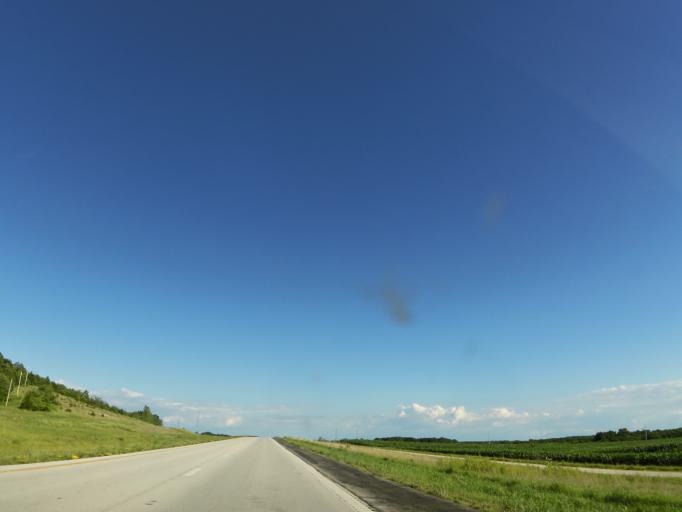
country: US
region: Missouri
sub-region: Pike County
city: Bowling Green
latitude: 39.4604
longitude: -91.2761
